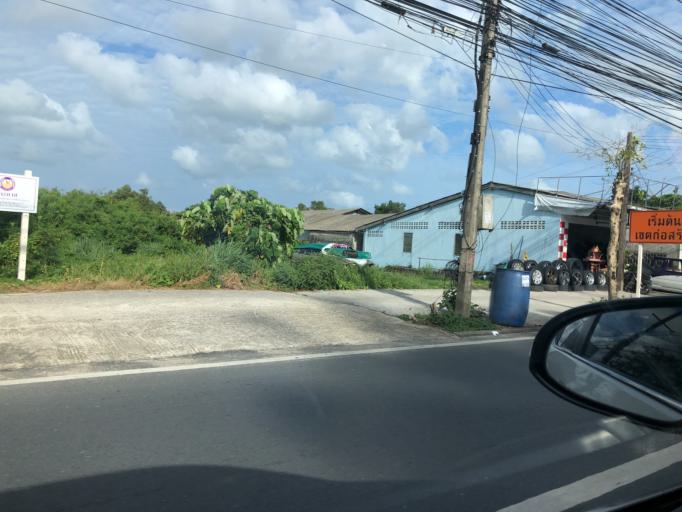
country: TH
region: Phuket
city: Ban Ko Kaeo
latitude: 7.9746
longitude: 98.3689
